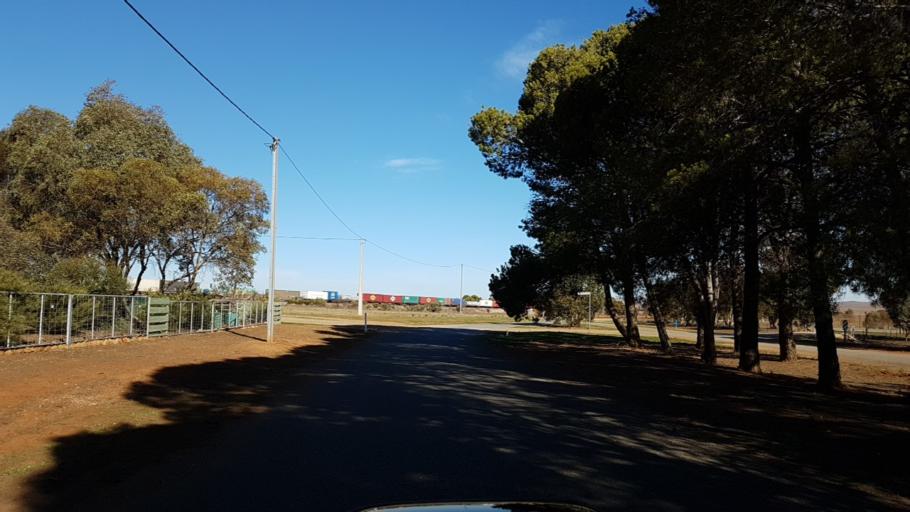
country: AU
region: South Australia
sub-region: Peterborough
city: Peterborough
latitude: -33.0315
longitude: 138.7500
